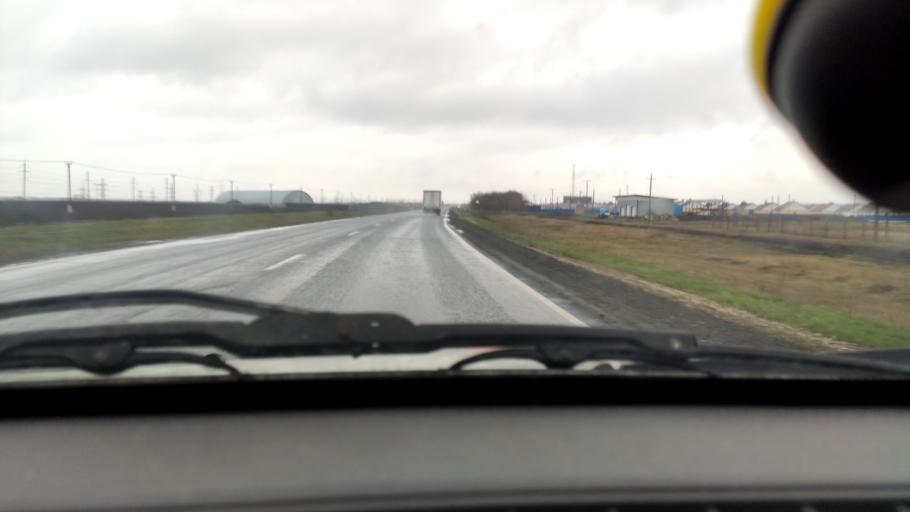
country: RU
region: Samara
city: Povolzhskiy
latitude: 53.6422
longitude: 49.6638
